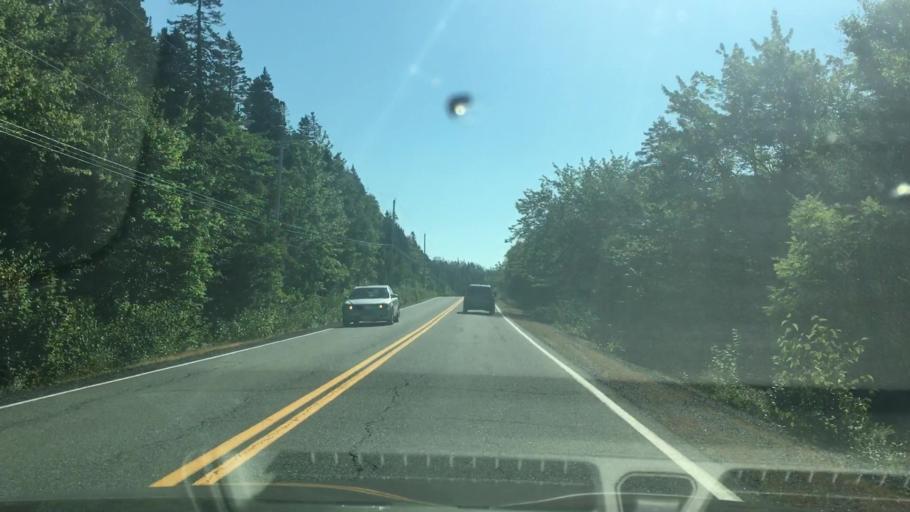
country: CA
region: Nova Scotia
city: Cole Harbour
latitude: 44.8128
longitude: -62.8404
